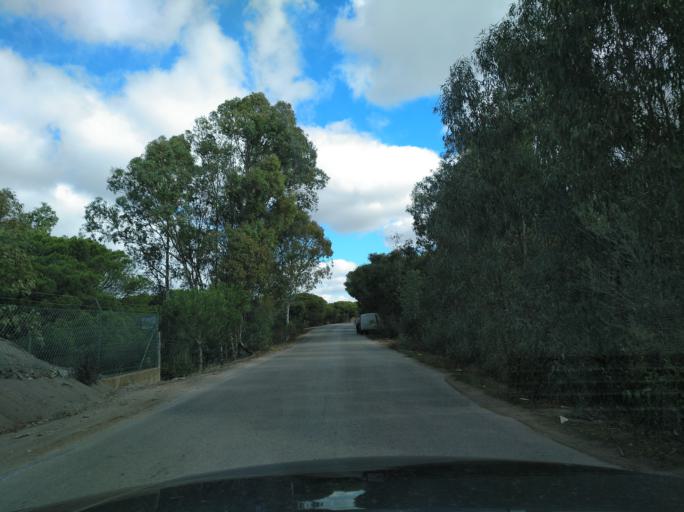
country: PT
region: Faro
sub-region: Vila Real de Santo Antonio
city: Monte Gordo
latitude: 37.1879
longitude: -7.4873
